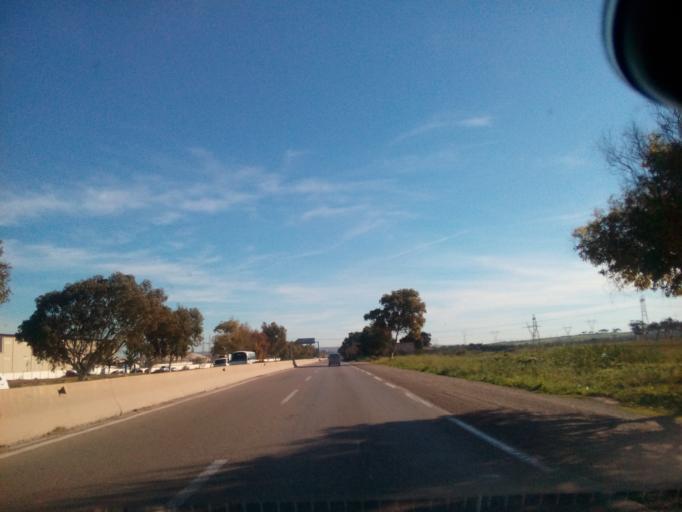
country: DZ
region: Oran
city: Ain el Bya
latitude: 35.7849
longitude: -0.1528
